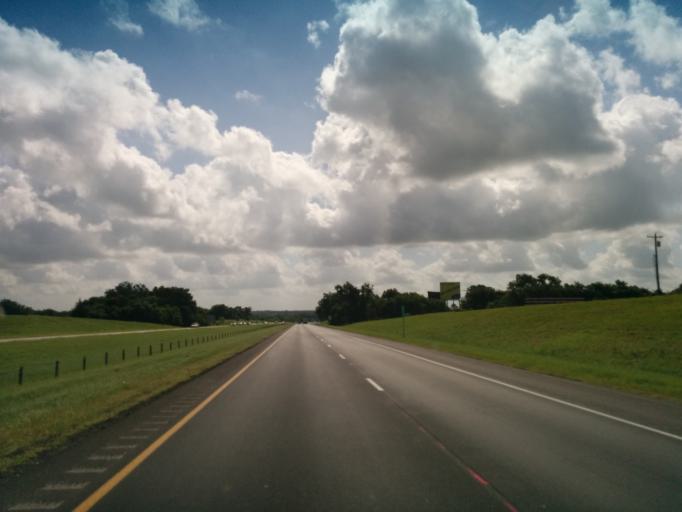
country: US
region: Texas
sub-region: Fayette County
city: Schulenburg
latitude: 29.6949
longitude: -96.8923
